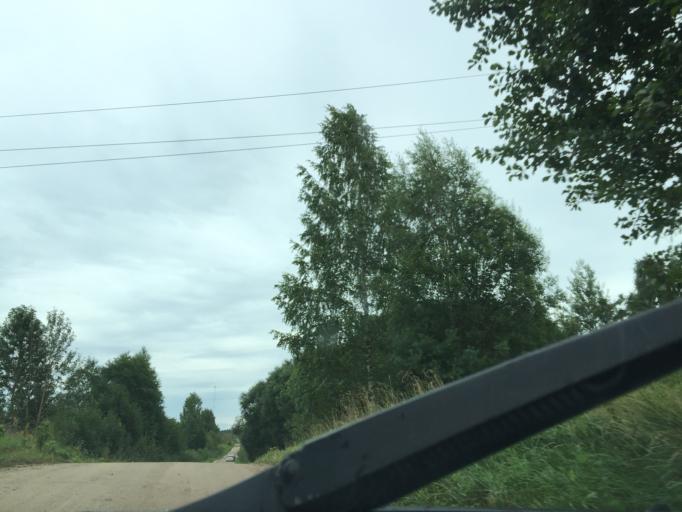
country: LV
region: Preilu Rajons
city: Jaunaglona
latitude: 56.2699
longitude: 27.0691
